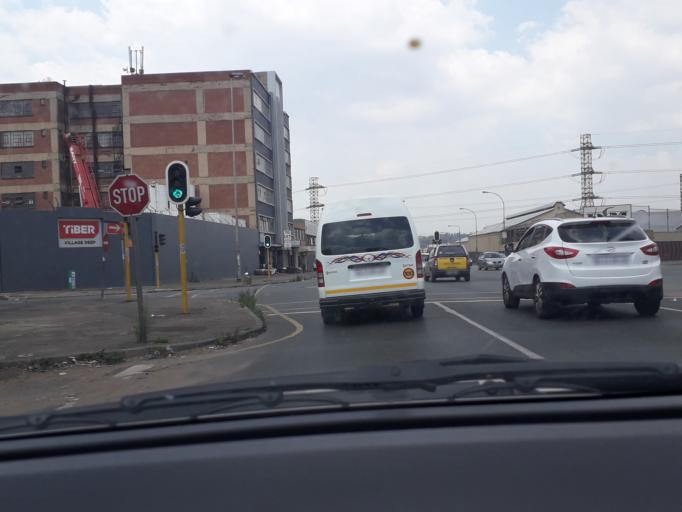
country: ZA
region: Gauteng
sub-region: City of Johannesburg Metropolitan Municipality
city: Johannesburg
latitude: -26.2234
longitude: 28.0436
